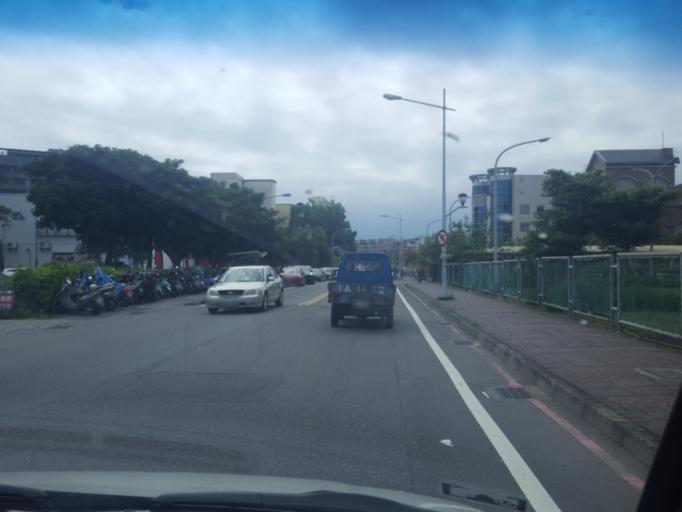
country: TW
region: Taiwan
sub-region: Yilan
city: Yilan
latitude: 24.7518
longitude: 121.7584
